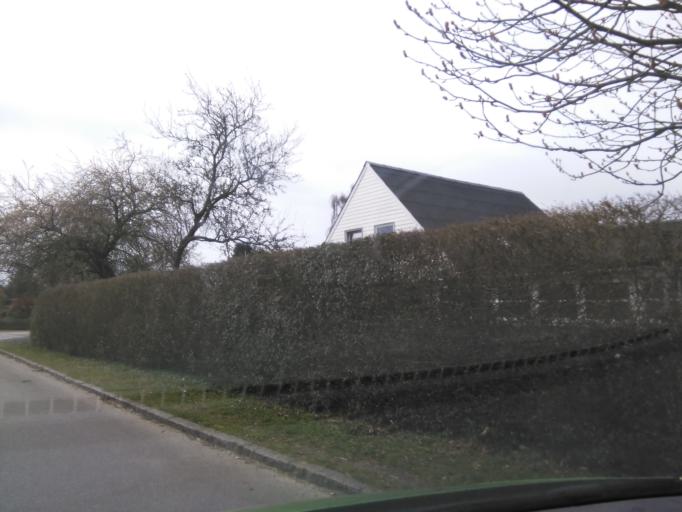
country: DK
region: Central Jutland
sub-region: Arhus Kommune
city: Malling
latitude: 55.9745
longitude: 10.2337
